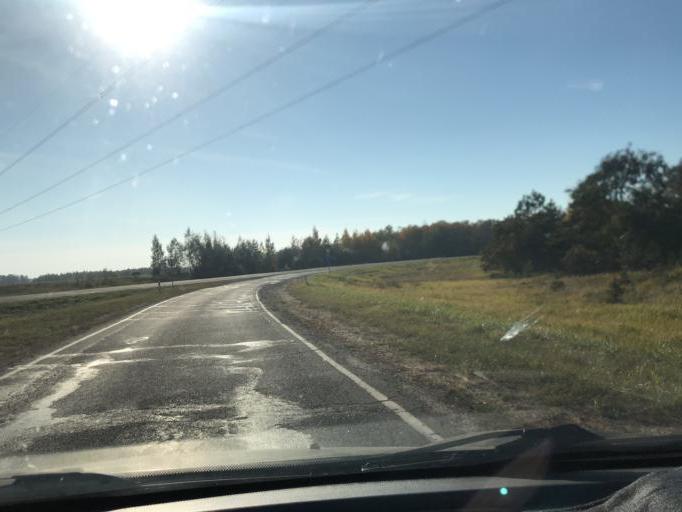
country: BY
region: Mogilev
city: Babruysk
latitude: 53.1059
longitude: 29.0536
